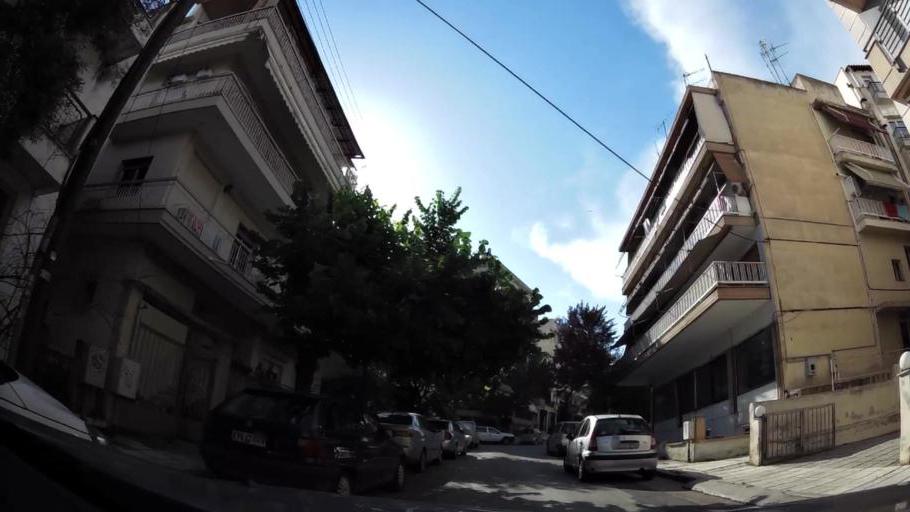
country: GR
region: Central Macedonia
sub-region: Nomos Thessalonikis
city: Kalamaria
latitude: 40.5684
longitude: 22.9592
